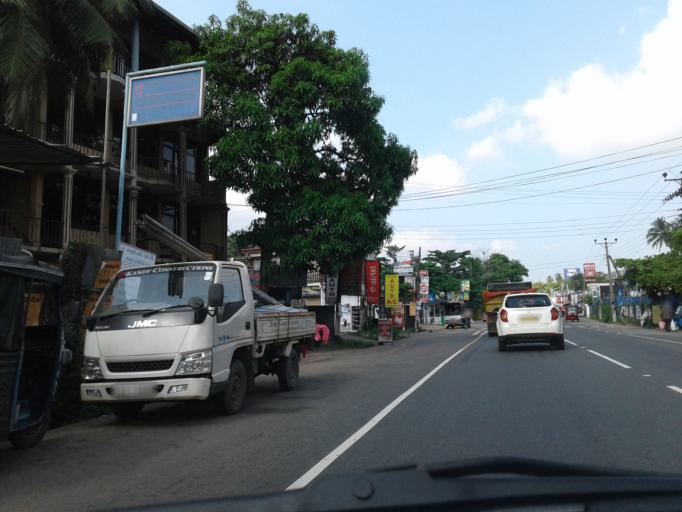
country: LK
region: Western
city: Battaramulla South
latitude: 6.9083
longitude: 79.9398
